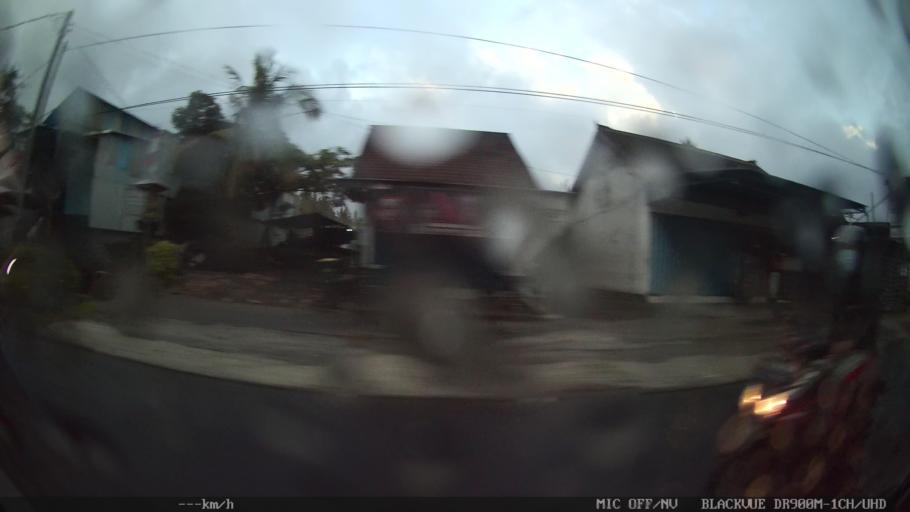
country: ID
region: Bali
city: Banjar Batur
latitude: -8.5955
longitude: 115.2149
